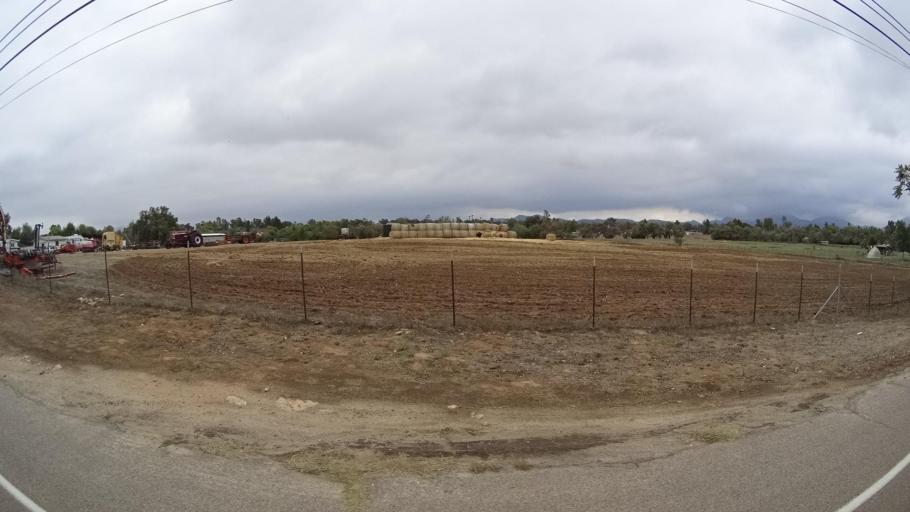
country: US
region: California
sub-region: San Diego County
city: Ramona
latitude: 33.0403
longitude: -116.8854
